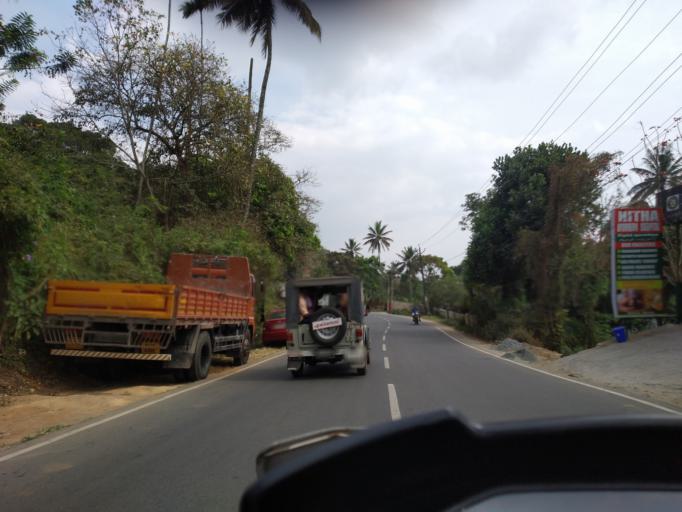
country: IN
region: Tamil Nadu
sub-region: Theni
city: Gudalur
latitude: 9.6105
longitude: 77.1629
